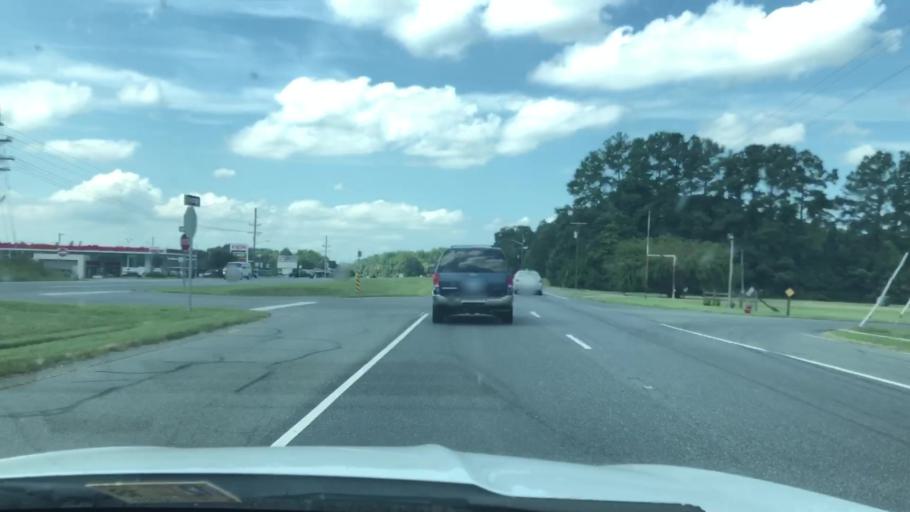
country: US
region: Virginia
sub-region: Richmond County
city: Warsaw
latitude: 37.9630
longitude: -76.7805
